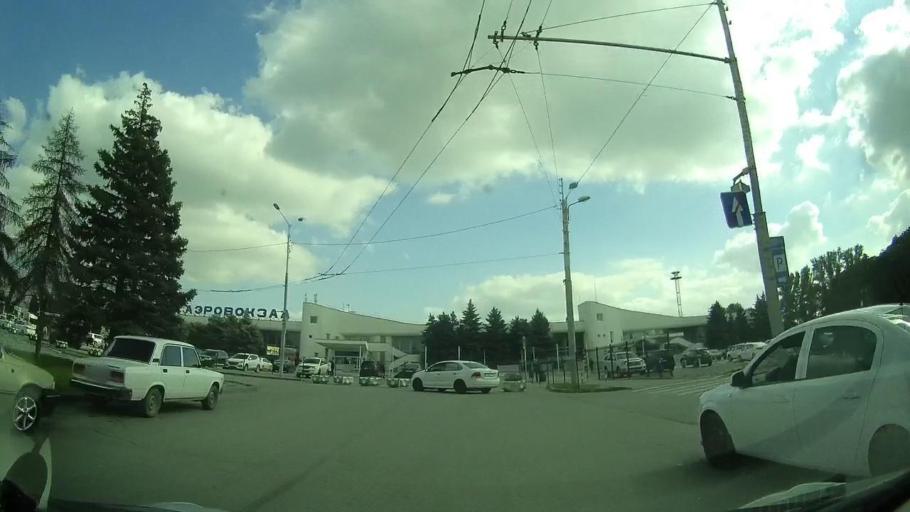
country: RU
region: Rostov
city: Imeni Chkalova
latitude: 47.2556
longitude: 39.8019
